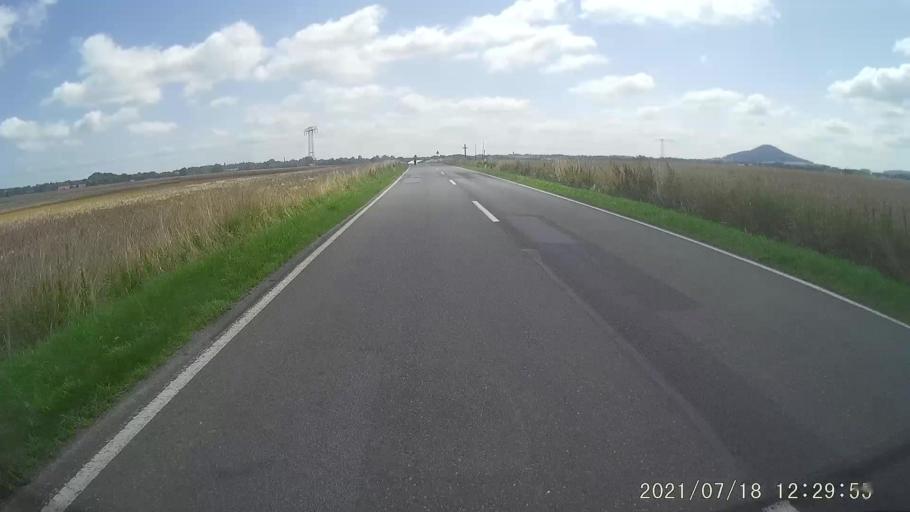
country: DE
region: Saxony
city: Markersdorf
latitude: 51.1688
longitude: 14.9163
